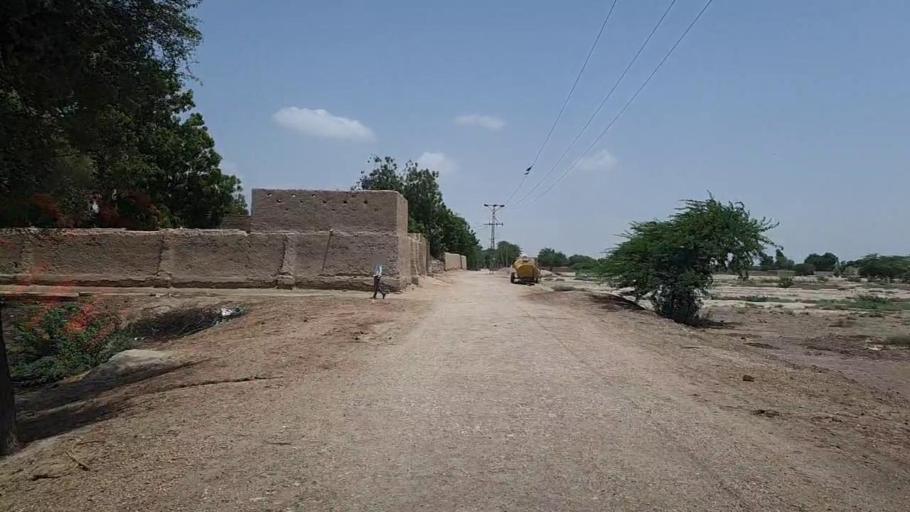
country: PK
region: Sindh
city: Pad Idan
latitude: 26.7531
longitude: 68.3069
